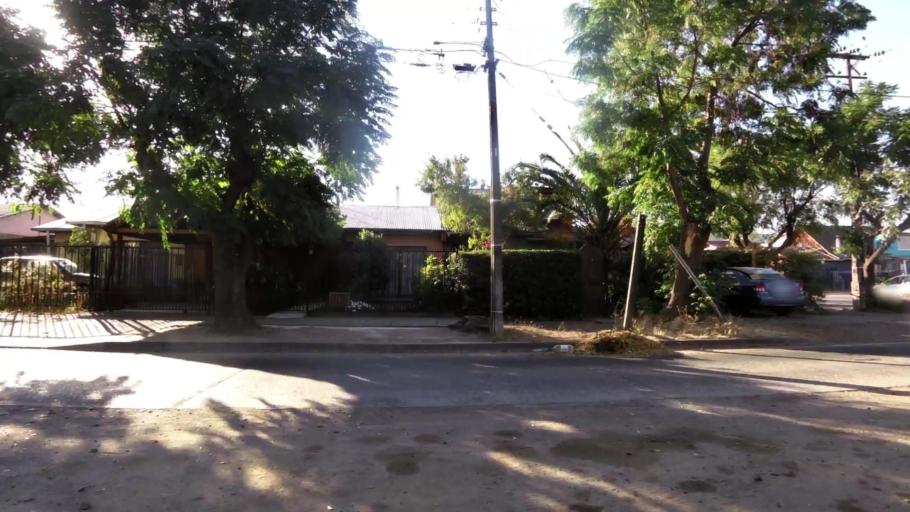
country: CL
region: Maule
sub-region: Provincia de Talca
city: Talca
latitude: -35.4372
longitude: -71.6865
